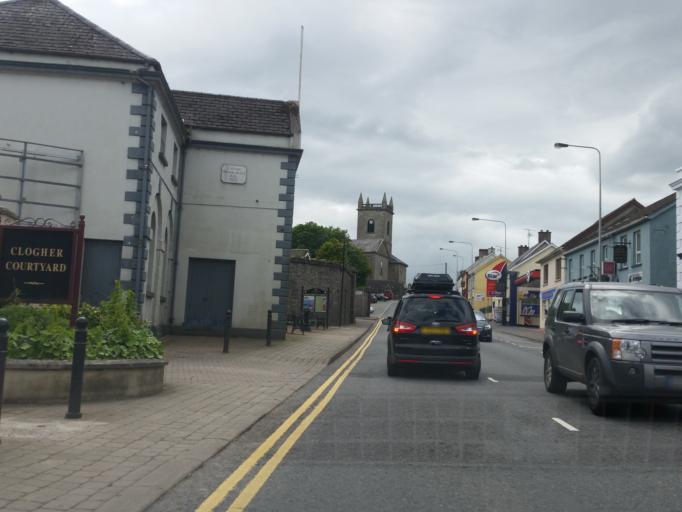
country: GB
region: Northern Ireland
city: Fivemiletown
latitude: 54.4116
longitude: -7.1706
